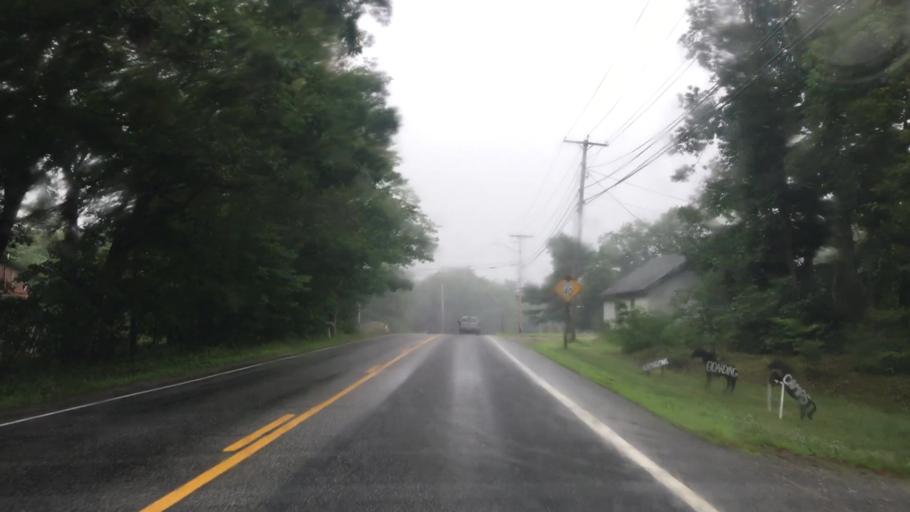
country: US
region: Maine
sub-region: Lincoln County
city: Boothbay
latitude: 43.9084
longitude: -69.6165
